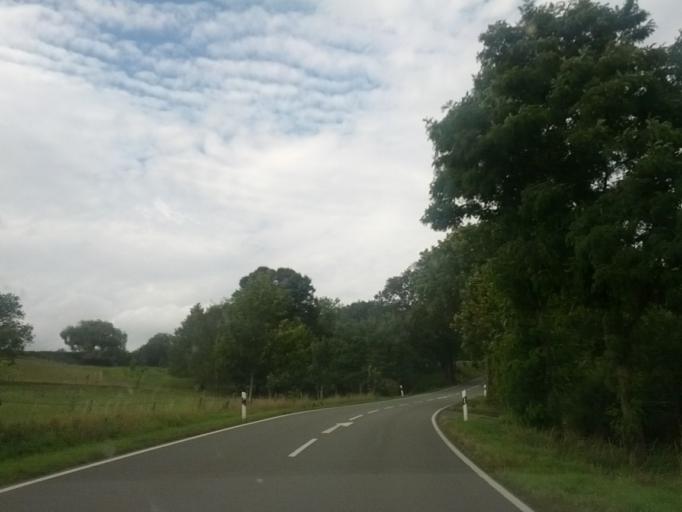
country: DE
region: Thuringia
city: Immelborn
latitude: 50.8248
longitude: 10.2766
